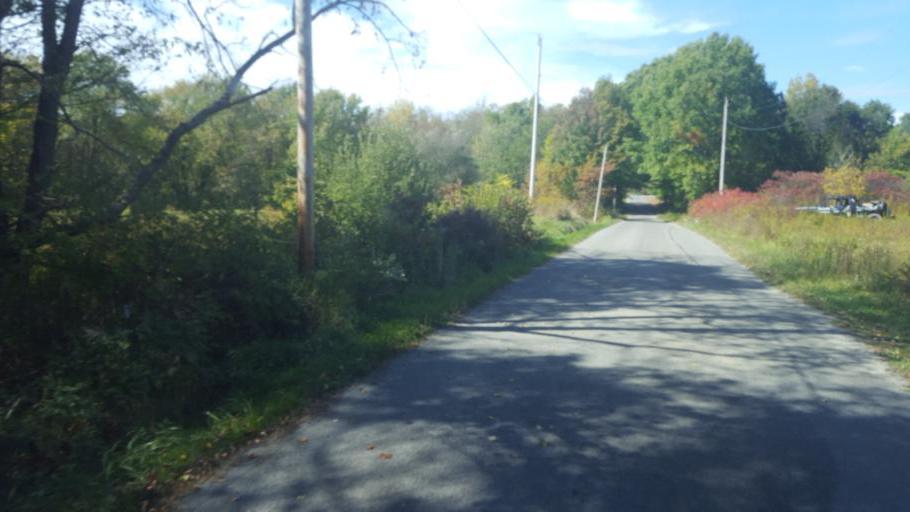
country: US
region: Pennsylvania
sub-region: Mercer County
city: Mercer
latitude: 41.3406
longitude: -80.2467
